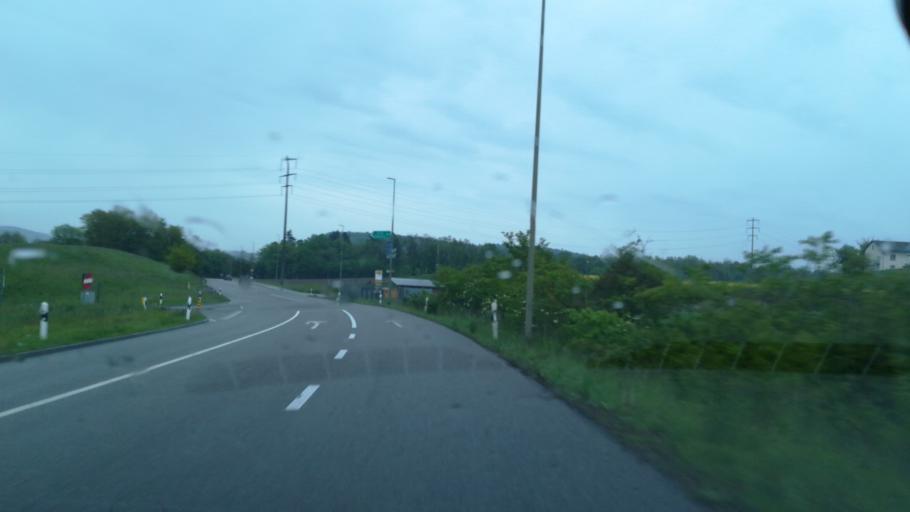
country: CH
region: Zurich
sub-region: Bezirk Buelach
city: Glattfelden
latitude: 47.5661
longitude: 8.4740
